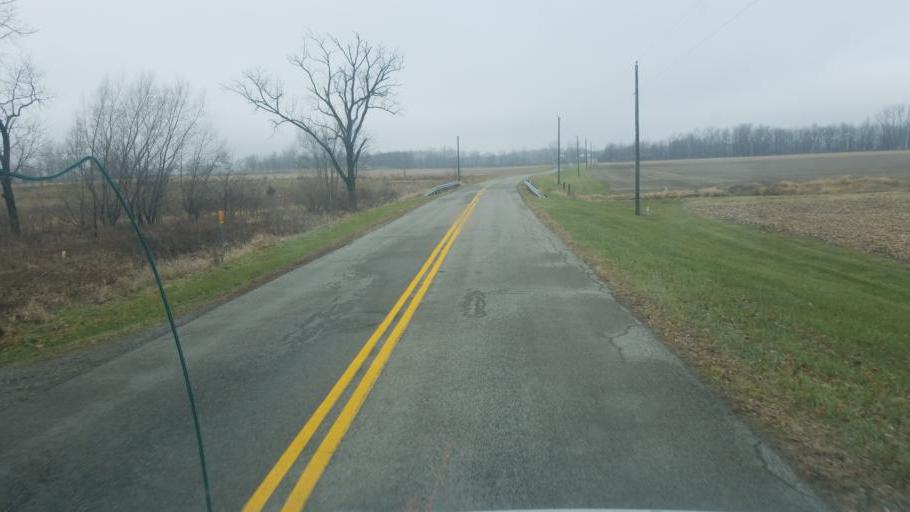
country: US
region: Ohio
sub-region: Champaign County
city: North Lewisburg
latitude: 40.2548
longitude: -83.5462
